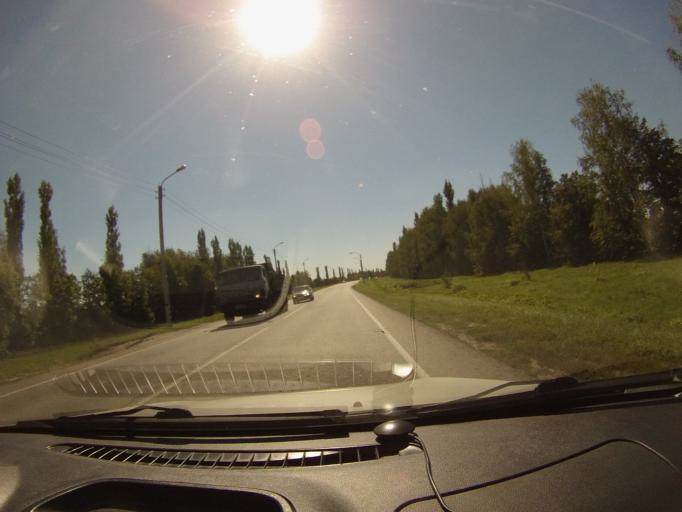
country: RU
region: Tambov
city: Donskoye
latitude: 52.7983
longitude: 41.4954
